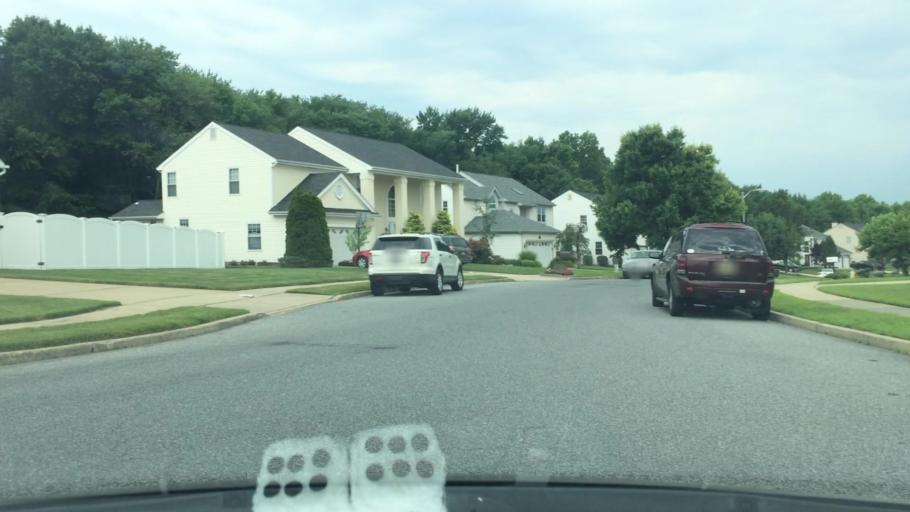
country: US
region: New Jersey
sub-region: Gloucester County
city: Turnersville
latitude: 39.7769
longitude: -75.0647
